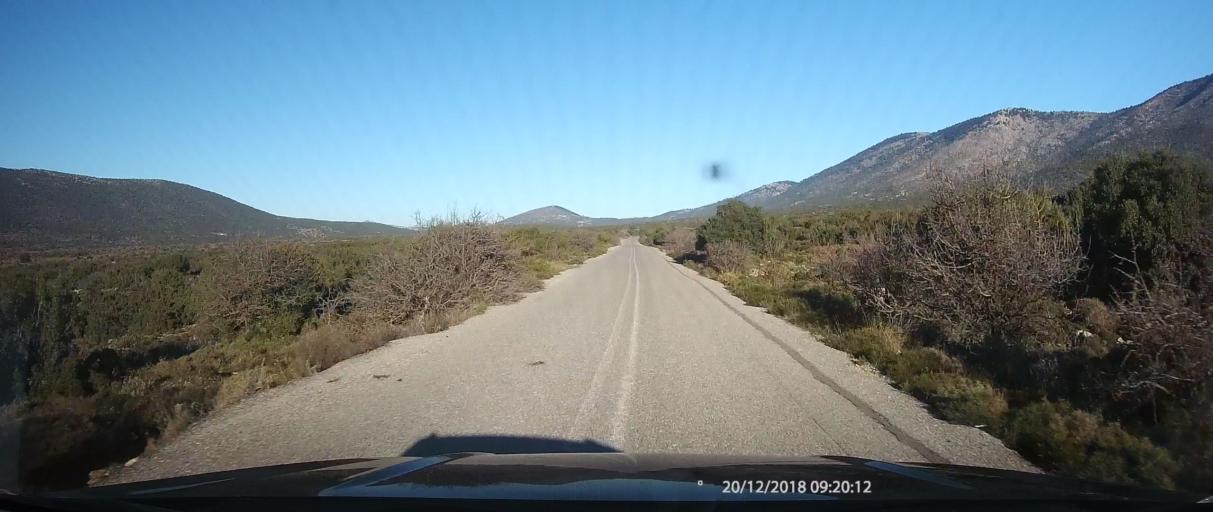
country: GR
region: Peloponnese
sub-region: Nomos Lakonias
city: Molaoi
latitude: 36.9263
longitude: 22.9275
